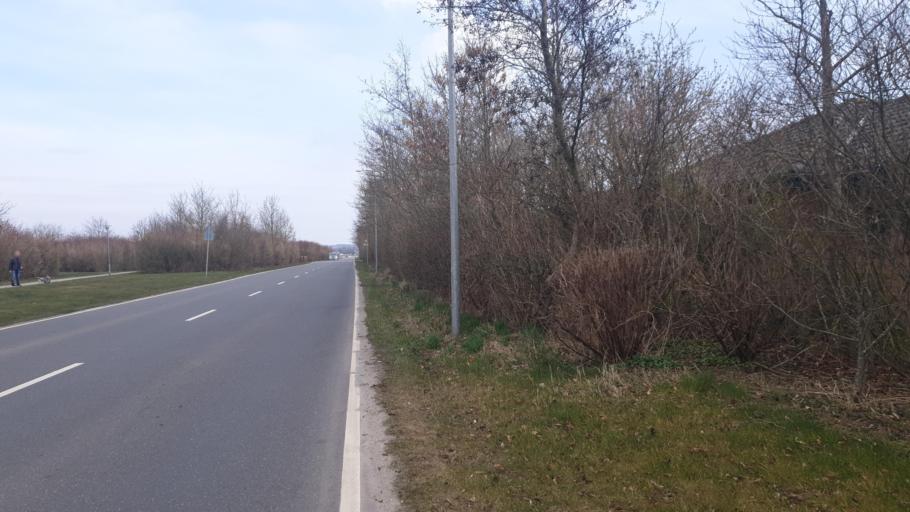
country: DK
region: Central Jutland
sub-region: Hedensted Kommune
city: Hedensted
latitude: 55.7656
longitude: 9.7130
